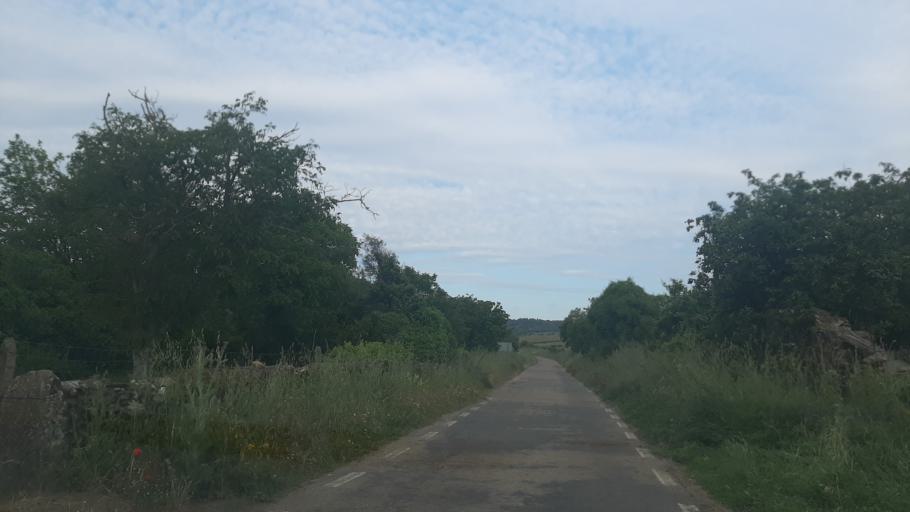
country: ES
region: Castille and Leon
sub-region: Provincia de Salamanca
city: Aldea del Obispo
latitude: 40.6519
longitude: -6.7625
